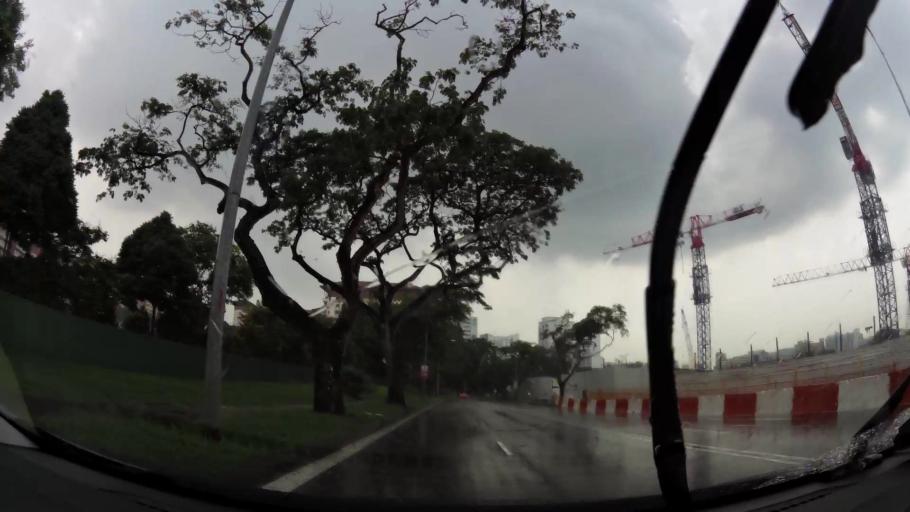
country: SG
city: Singapore
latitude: 1.3376
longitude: 103.8768
